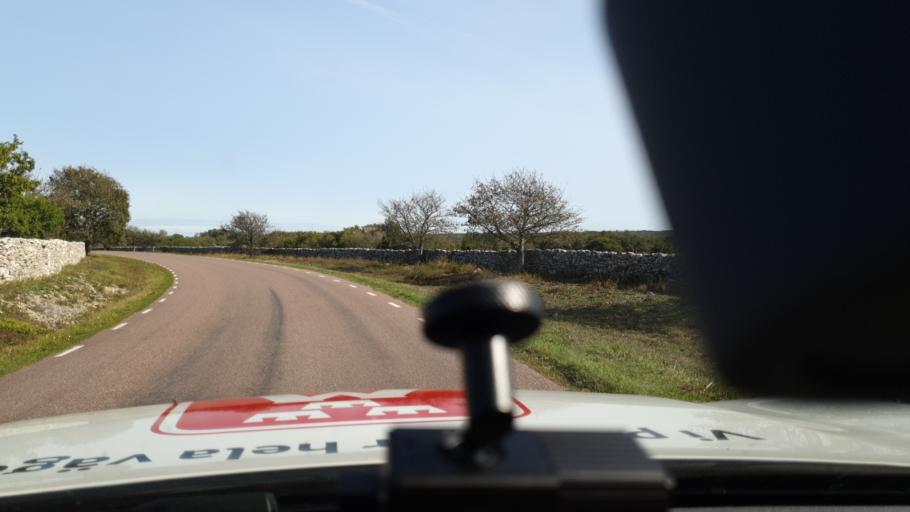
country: SE
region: Gotland
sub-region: Gotland
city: Hemse
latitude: 56.9165
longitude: 18.1526
